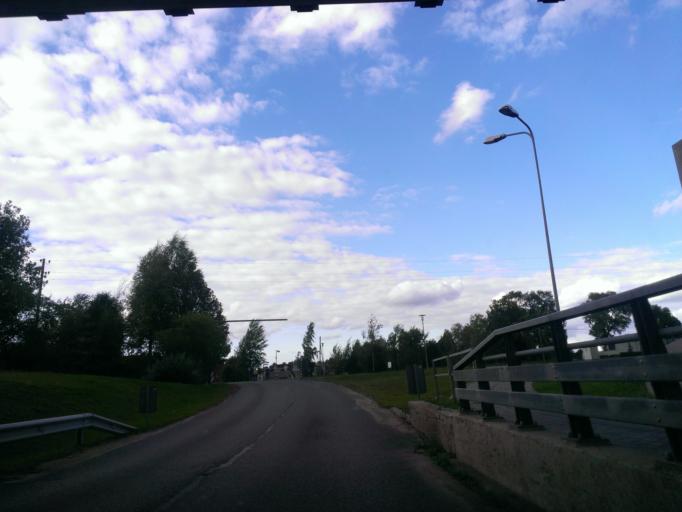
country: LV
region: Sigulda
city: Sigulda
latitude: 57.1556
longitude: 24.8749
